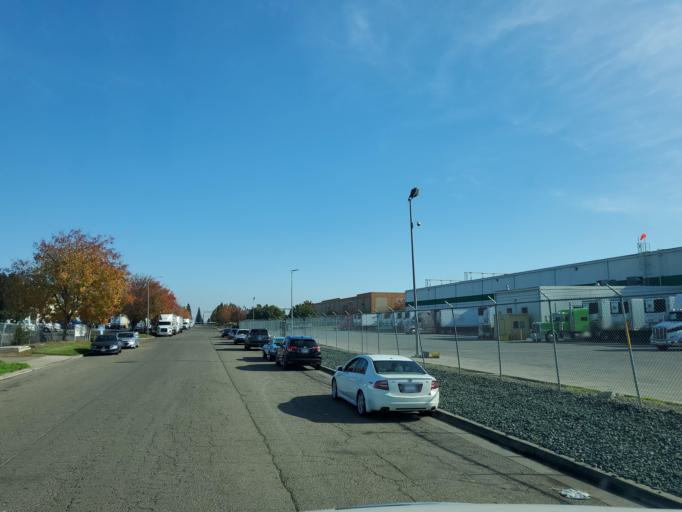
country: US
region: California
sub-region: San Joaquin County
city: Kennedy
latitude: 37.9114
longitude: -121.2184
